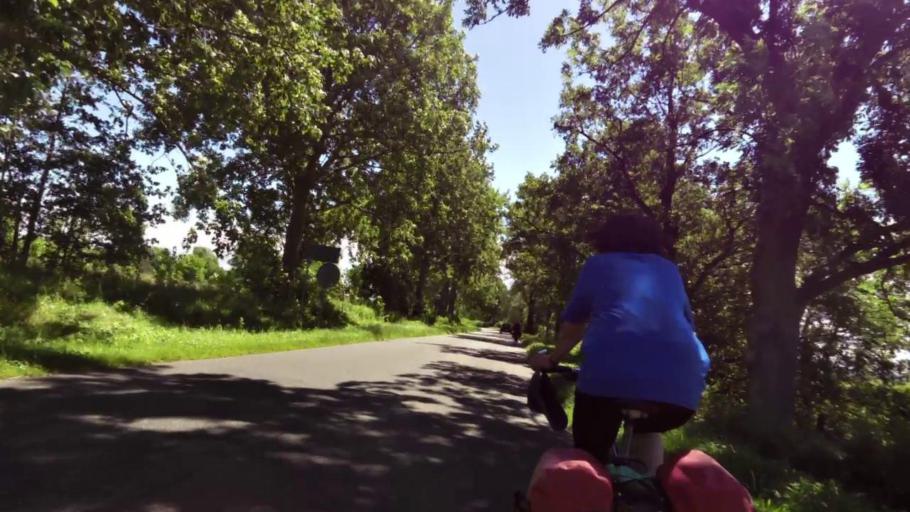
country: PL
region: West Pomeranian Voivodeship
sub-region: Koszalin
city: Koszalin
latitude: 54.3006
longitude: 16.2031
